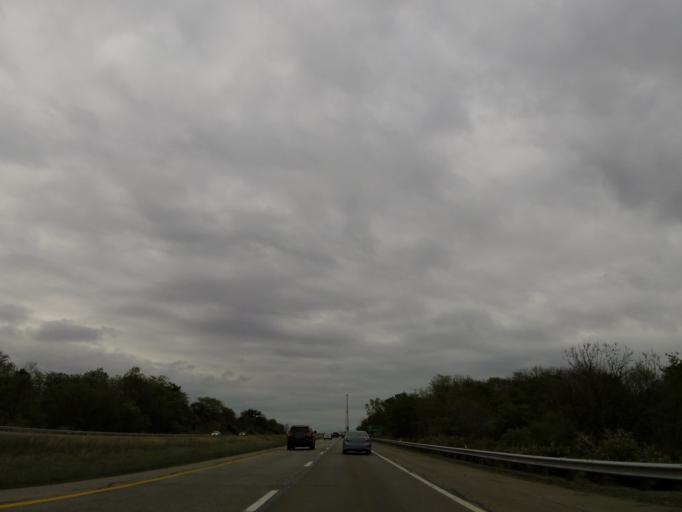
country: US
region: Ohio
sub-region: Madison County
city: Mount Sterling
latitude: 39.7641
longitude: -83.2893
